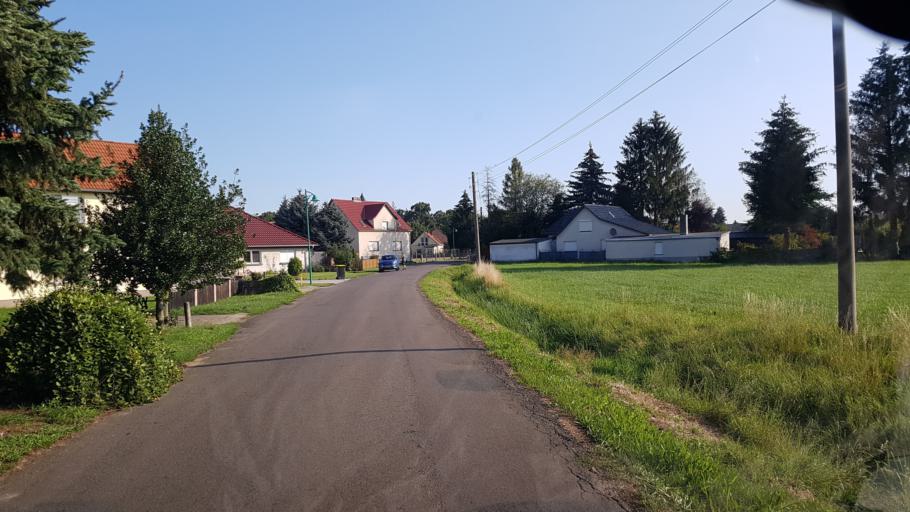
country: DE
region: Brandenburg
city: Luckau
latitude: 51.8006
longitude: 13.6482
